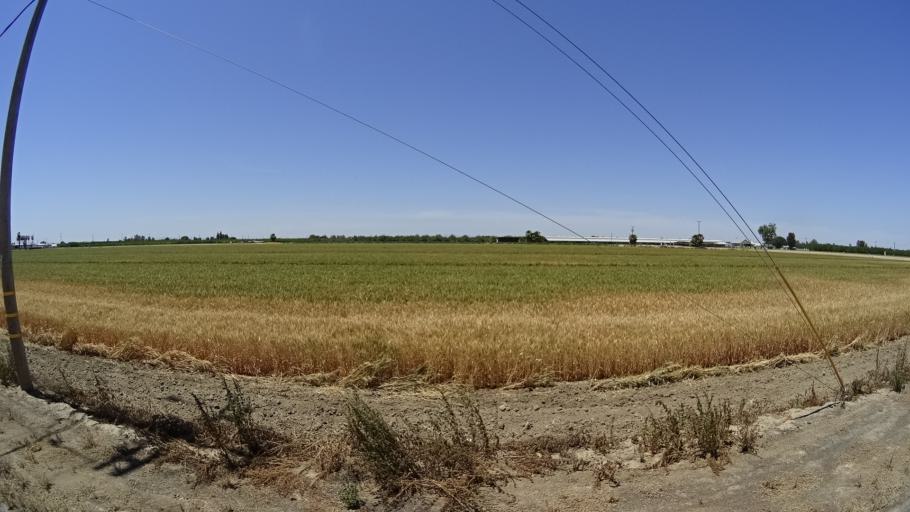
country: US
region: California
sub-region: Kings County
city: Armona
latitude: 36.3181
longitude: -119.7180
